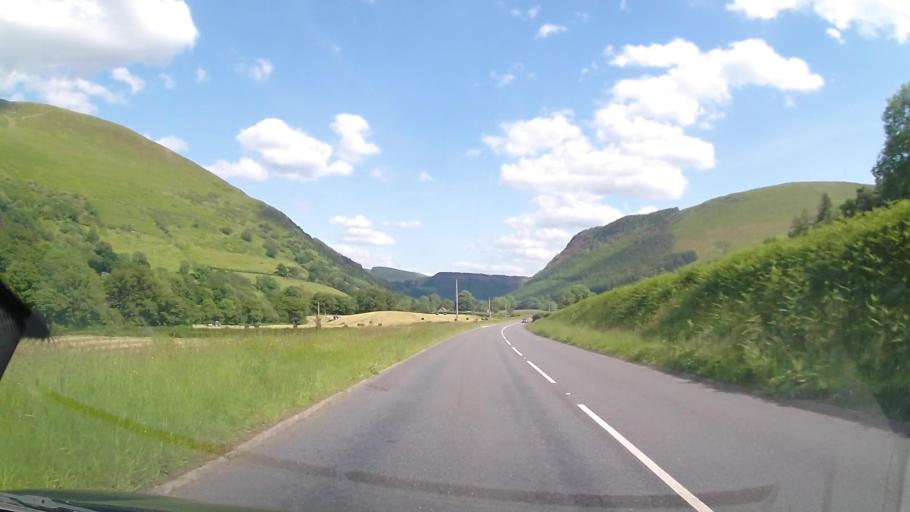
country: GB
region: Wales
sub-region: Gwynedd
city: Corris
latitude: 52.7314
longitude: -3.7183
